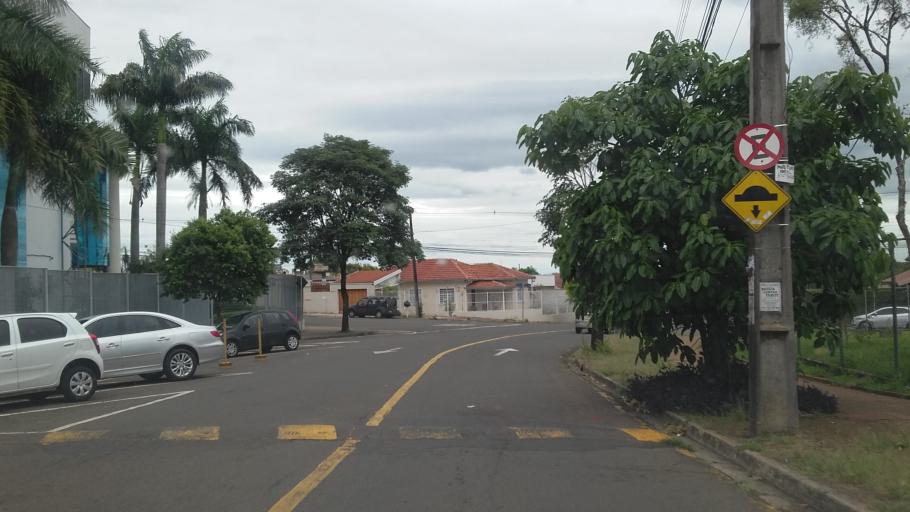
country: BR
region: Parana
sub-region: Londrina
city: Londrina
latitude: -23.3022
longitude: -51.1809
